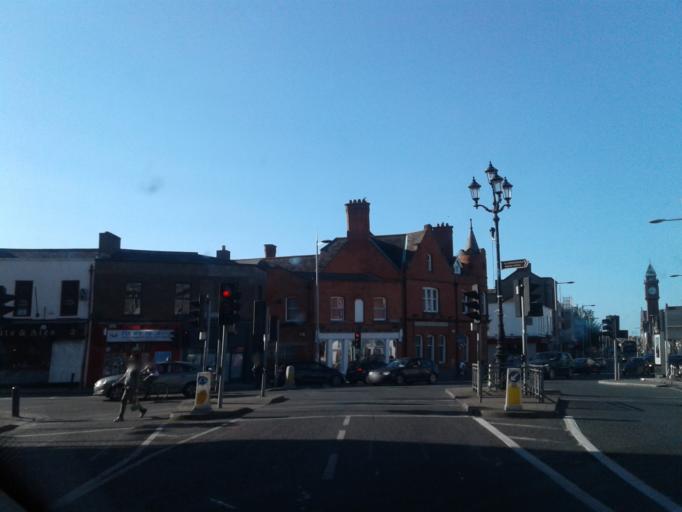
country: IE
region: Leinster
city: Rathmines
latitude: 53.3215
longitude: -6.2658
